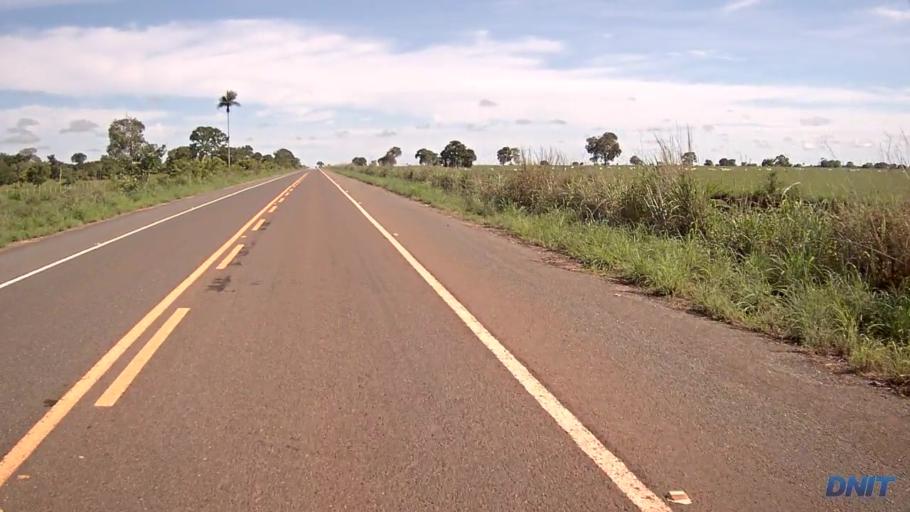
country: BR
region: Goias
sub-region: Sao Miguel Do Araguaia
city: Sao Miguel do Araguaia
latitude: -13.4472
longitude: -50.1217
